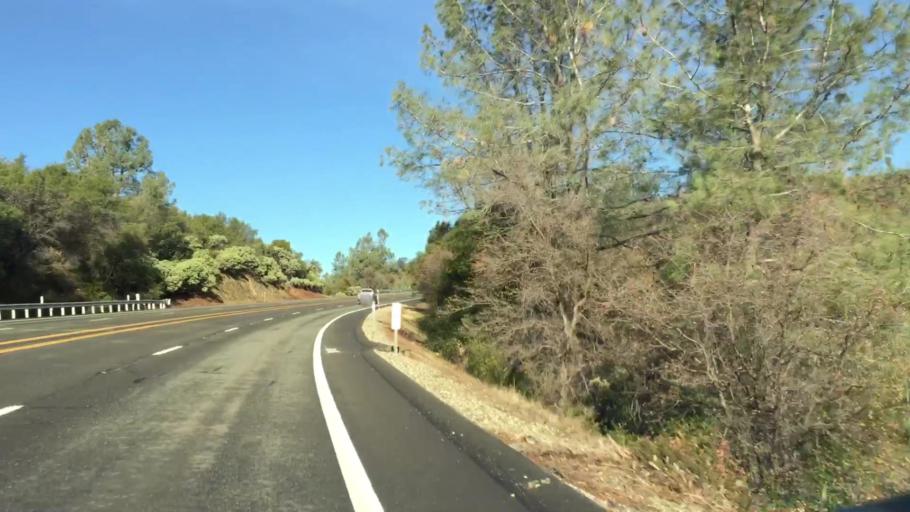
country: US
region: California
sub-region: Butte County
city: Paradise
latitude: 39.6802
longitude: -121.5458
